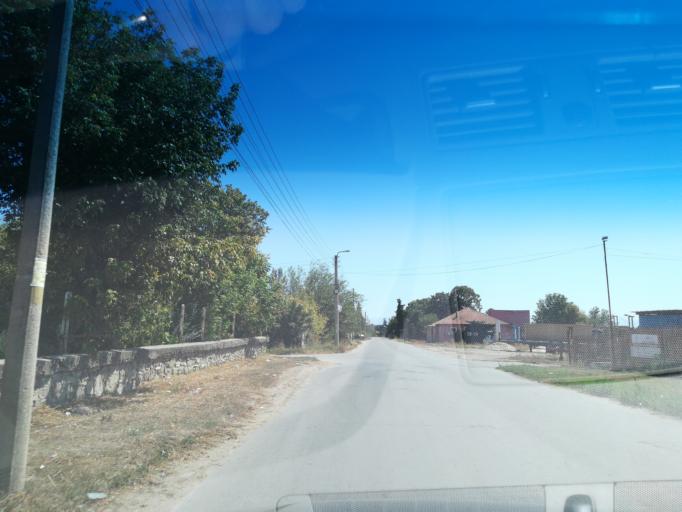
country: BG
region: Pazardzhik
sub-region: Obshtina Pazardzhik
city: Pazardzhik
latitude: 42.2717
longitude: 24.4012
